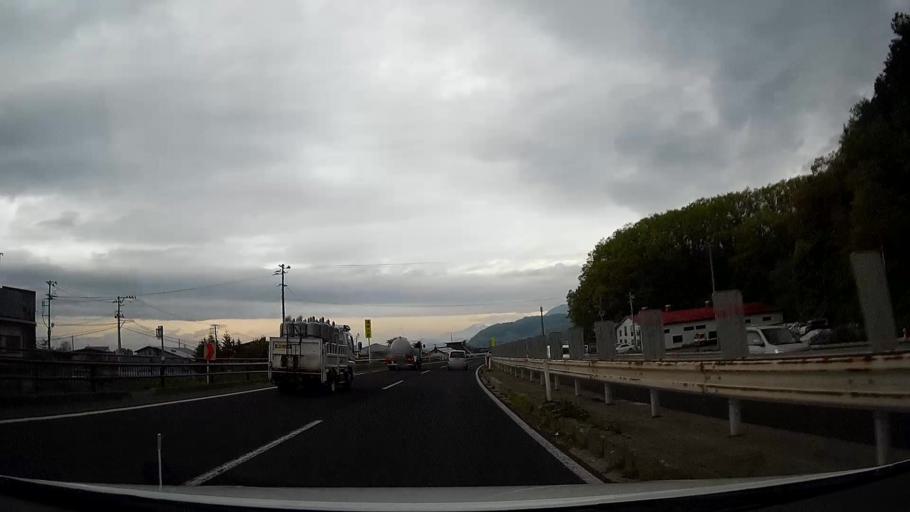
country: JP
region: Yamagata
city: Yamagata-shi
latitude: 38.2544
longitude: 140.3548
